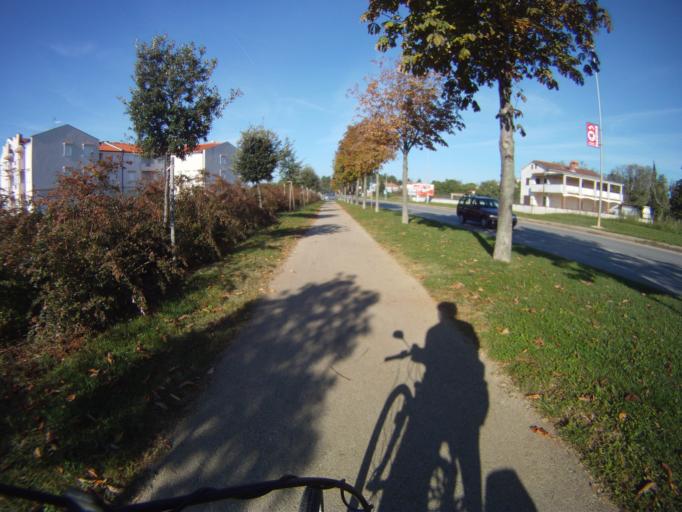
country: HR
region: Istarska
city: Novigrad
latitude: 45.3207
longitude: 13.5670
